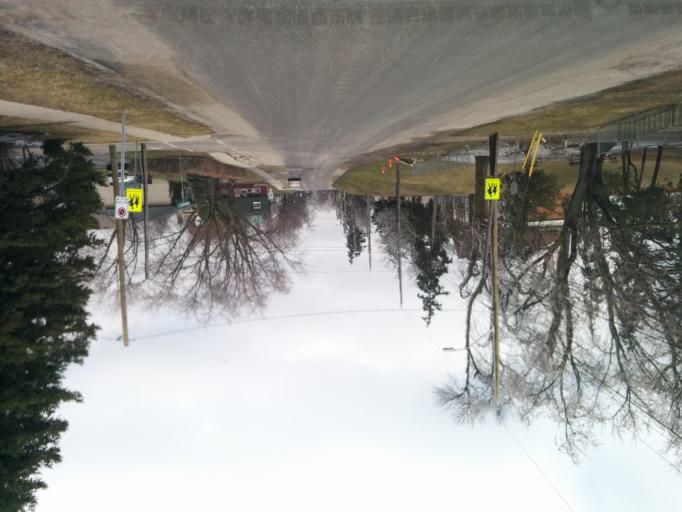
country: CA
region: Ontario
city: Waterloo
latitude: 43.5360
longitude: -80.5554
